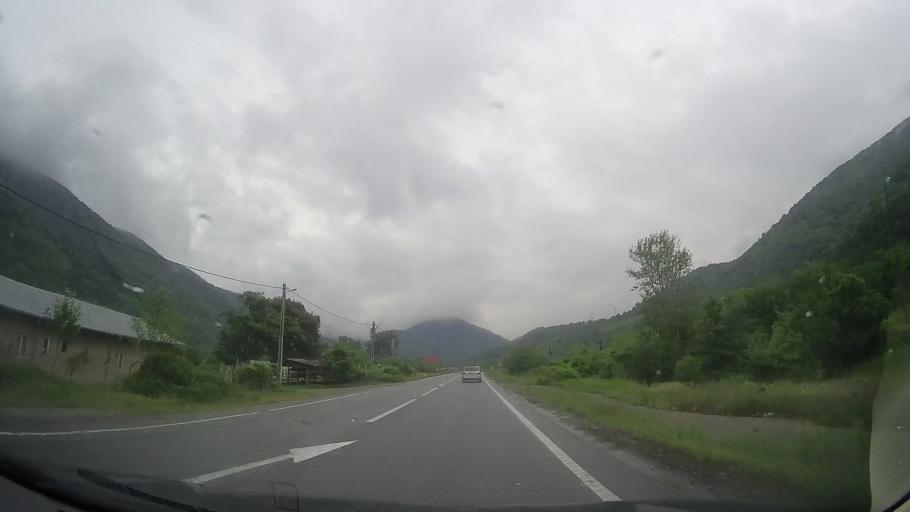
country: RO
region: Caras-Severin
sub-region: Oras Baile Herculane
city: Baile Herculane
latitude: 44.8775
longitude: 22.3844
